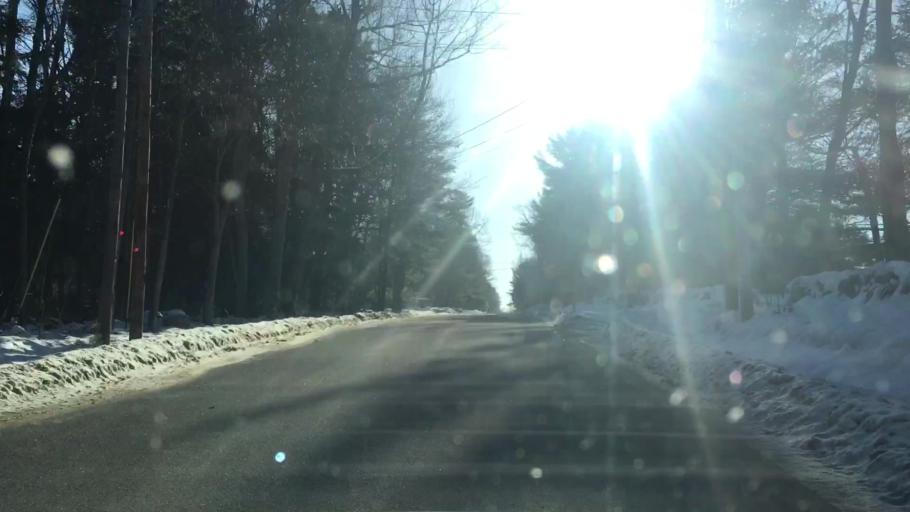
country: US
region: Maine
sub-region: Oxford County
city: Paris
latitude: 44.2755
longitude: -70.5072
